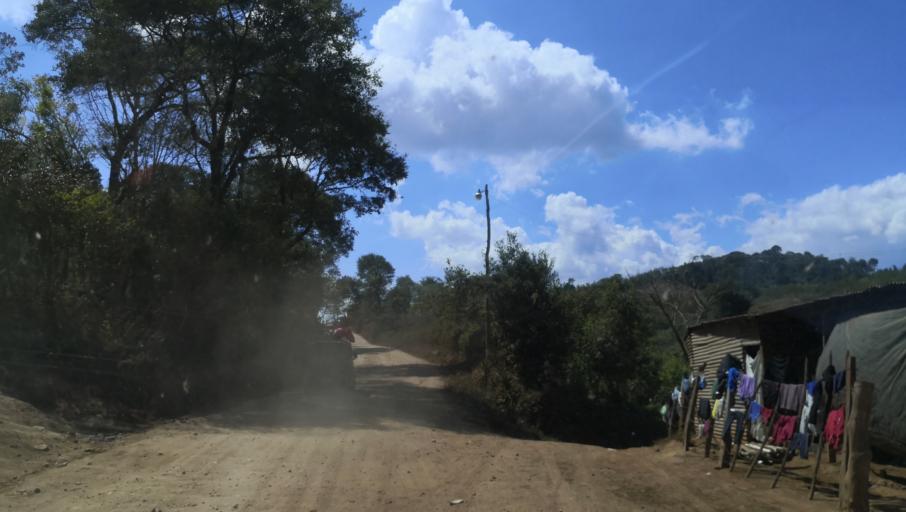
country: GT
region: Jalapa
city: San Carlos Alzatate
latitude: 14.4040
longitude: -89.9792
